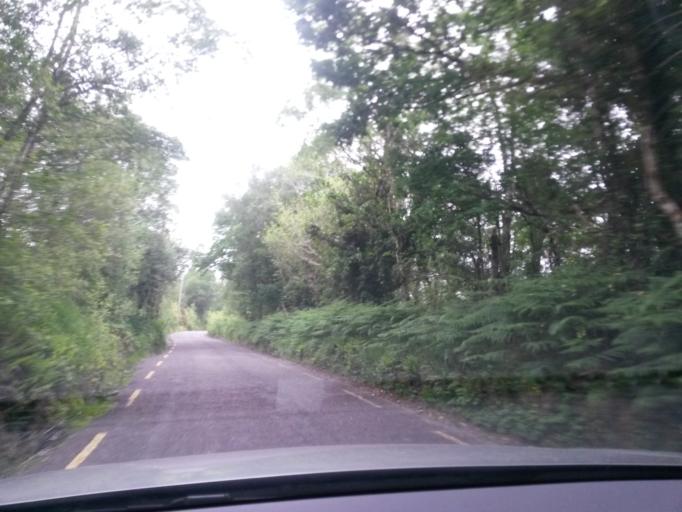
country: IE
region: Munster
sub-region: Ciarrai
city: Killorglin
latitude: 52.0051
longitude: -9.8340
